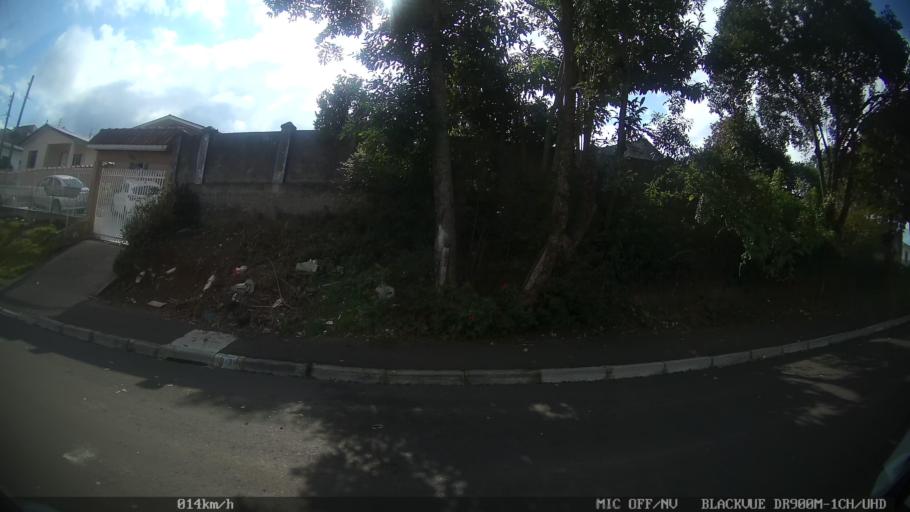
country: BR
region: Parana
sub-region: Colombo
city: Colombo
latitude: -25.3569
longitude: -49.1871
